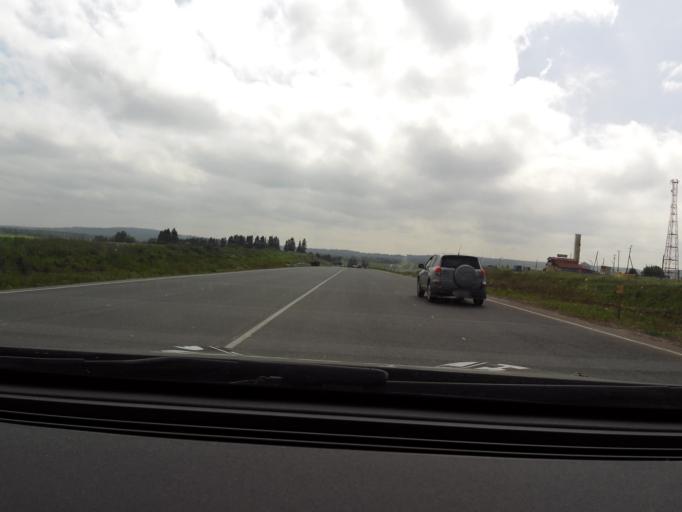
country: RU
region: Perm
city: Zvezdnyy
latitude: 57.7920
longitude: 56.3356
